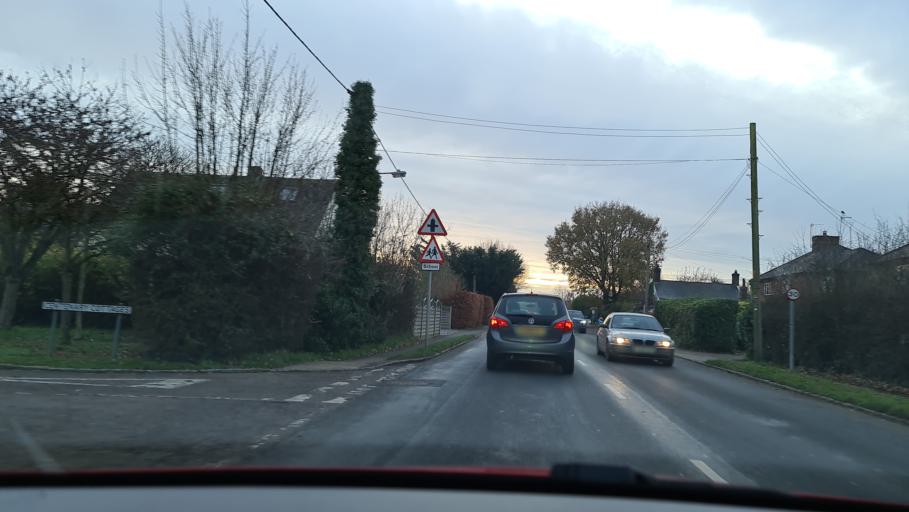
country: GB
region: England
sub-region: Buckinghamshire
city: Princes Risborough
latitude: 51.7398
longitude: -0.8616
